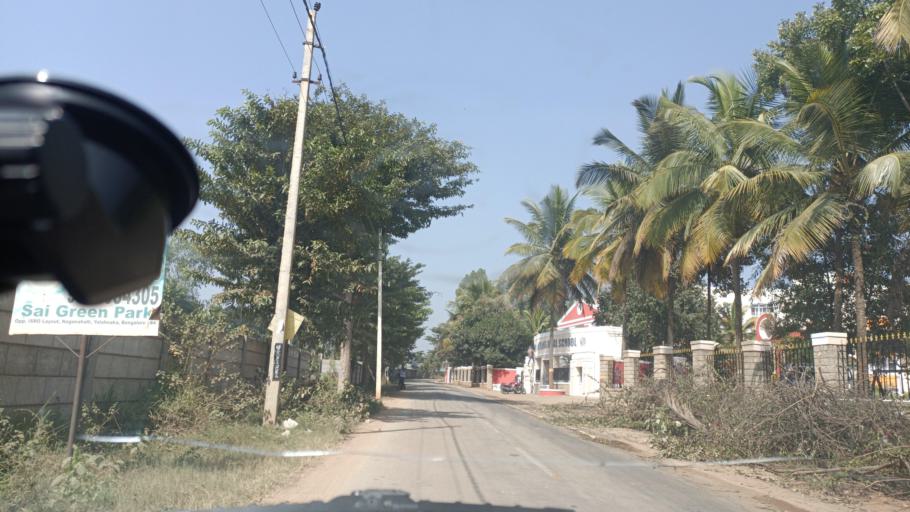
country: IN
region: Karnataka
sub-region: Bangalore Urban
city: Yelahanka
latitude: 13.1229
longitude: 77.6016
